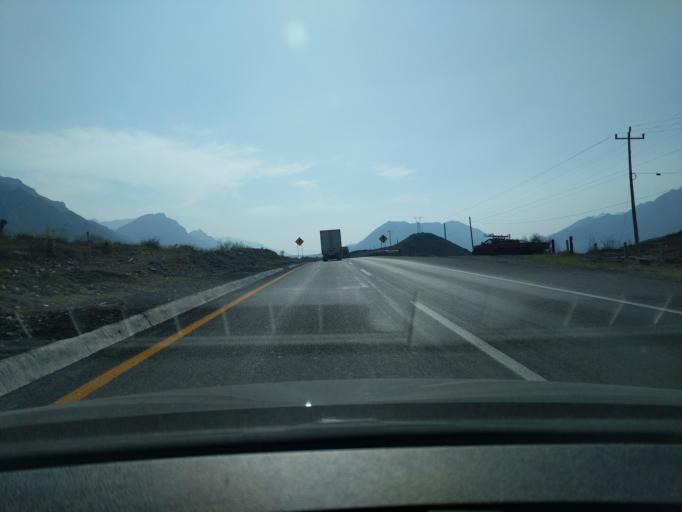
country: MX
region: Nuevo Leon
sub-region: Garcia
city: Las Torres de Guadalupe
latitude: 25.6825
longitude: -100.6621
